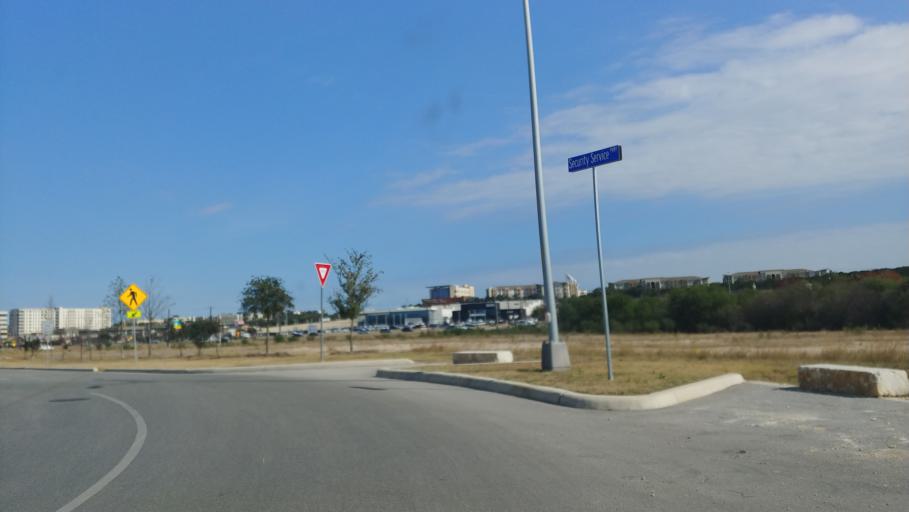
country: US
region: Texas
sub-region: Bexar County
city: Shavano Park
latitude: 29.5814
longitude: -98.5998
